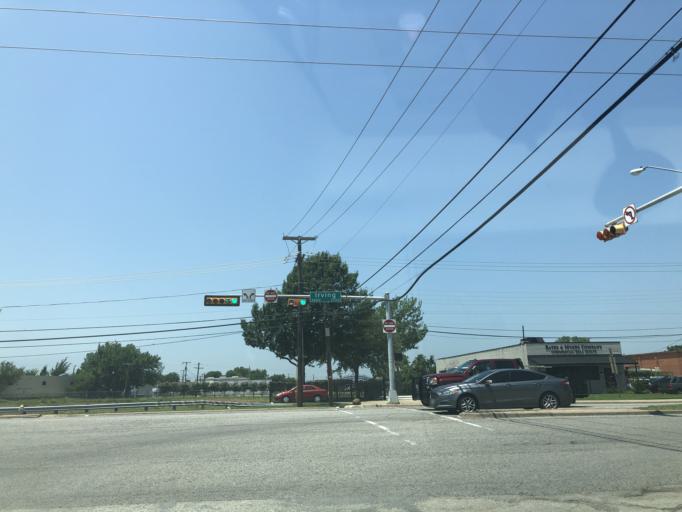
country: US
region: Texas
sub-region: Dallas County
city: Dallas
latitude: 32.8032
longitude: -96.8435
